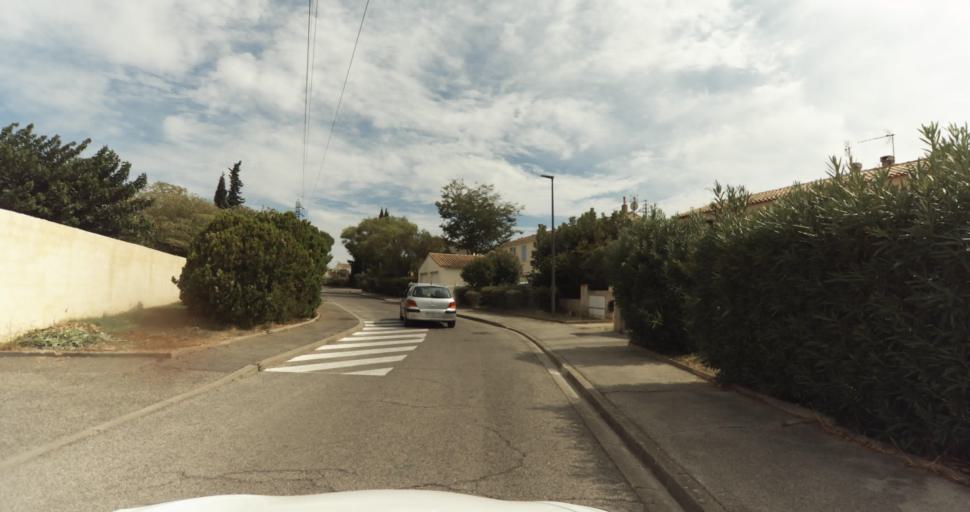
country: FR
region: Provence-Alpes-Cote d'Azur
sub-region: Departement des Bouches-du-Rhone
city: Miramas
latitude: 43.5733
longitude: 4.9963
